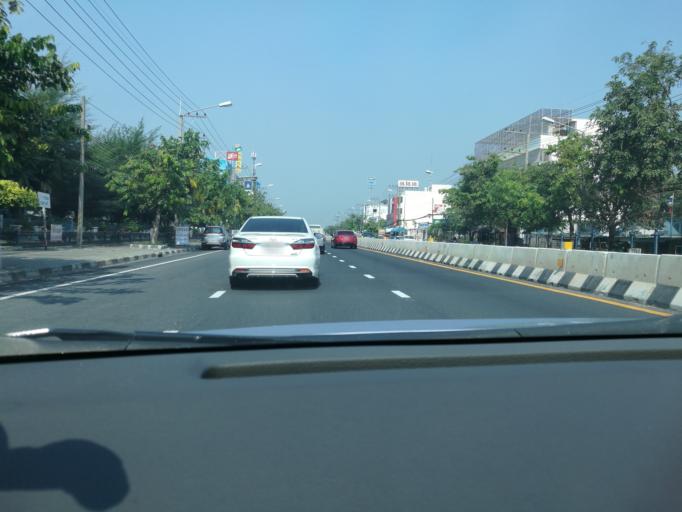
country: TH
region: Sara Buri
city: Saraburi
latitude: 14.5431
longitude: 100.9092
